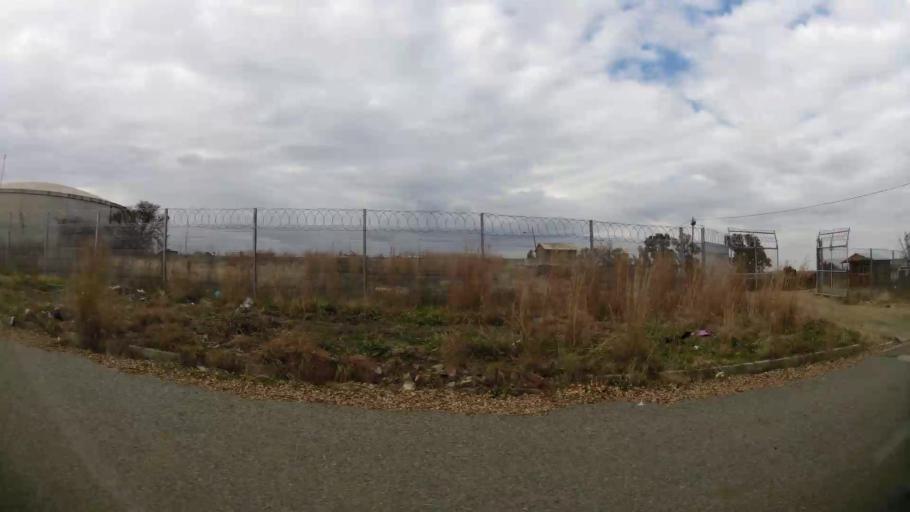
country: ZA
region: Orange Free State
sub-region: Fezile Dabi District Municipality
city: Kroonstad
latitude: -27.6507
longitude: 27.2336
